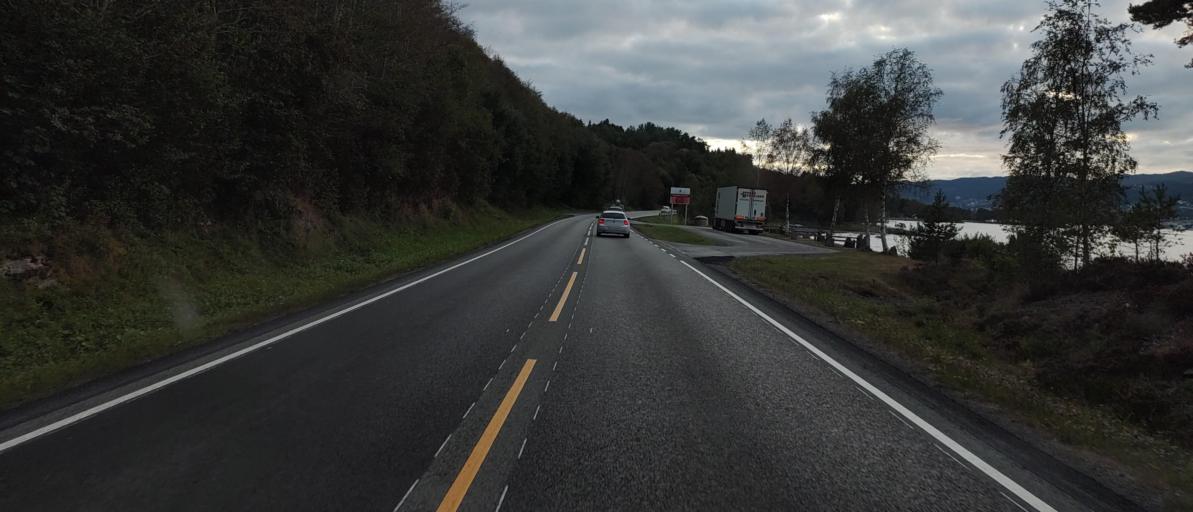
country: NO
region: More og Romsdal
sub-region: Molde
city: Molde
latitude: 62.7352
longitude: 7.3191
